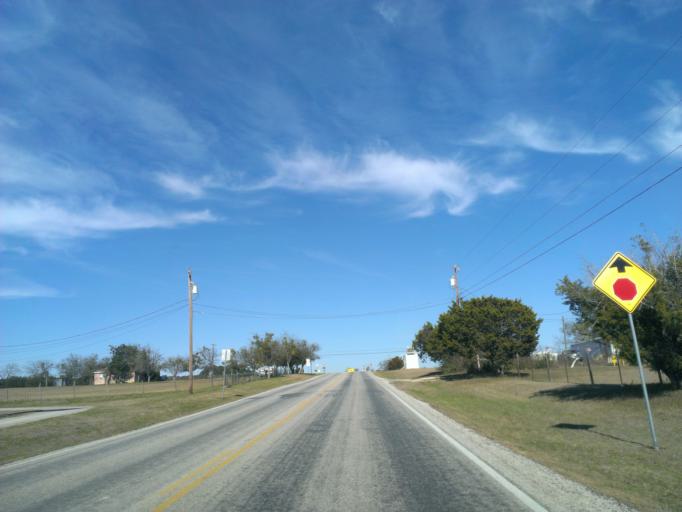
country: US
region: Texas
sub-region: Bell County
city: Nolanville
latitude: 31.0871
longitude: -97.6071
